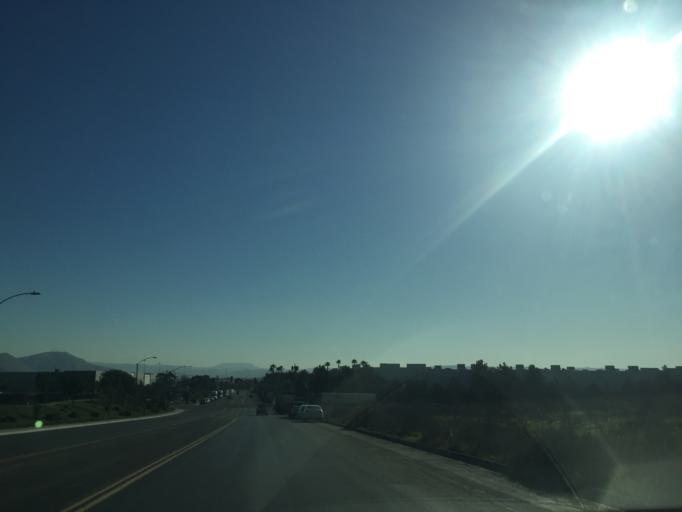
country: MX
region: Baja California
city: Tijuana
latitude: 32.5618
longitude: -116.9280
